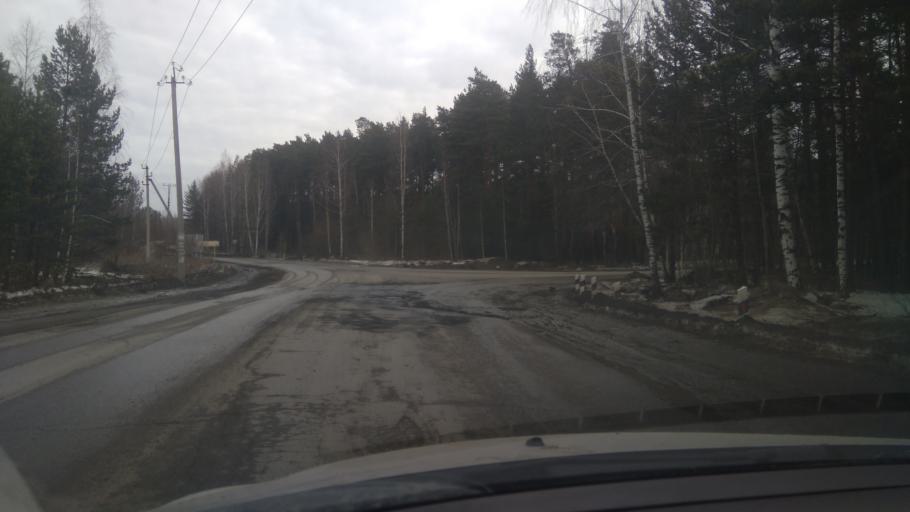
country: RU
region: Sverdlovsk
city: Severka
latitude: 56.8329
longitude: 60.3911
